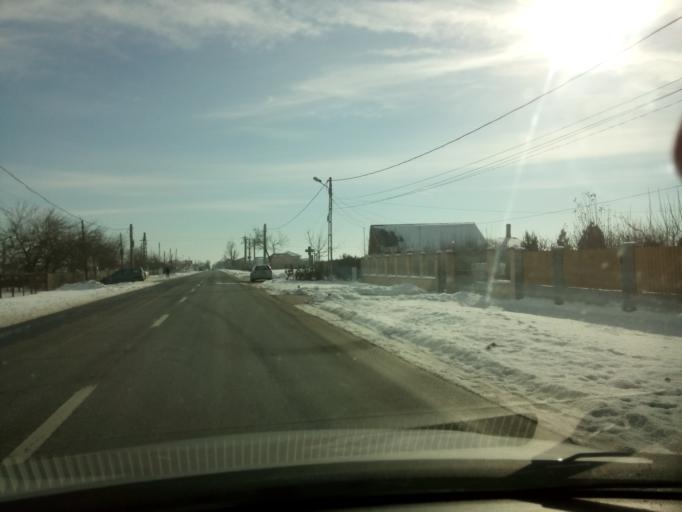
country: RO
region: Calarasi
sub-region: Comuna Frumusani
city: Frumusani
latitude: 44.2926
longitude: 26.3170
